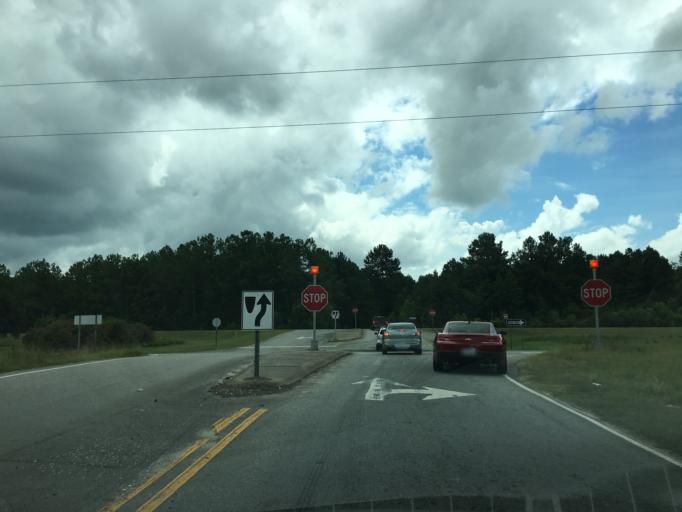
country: US
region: North Carolina
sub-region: Brunswick County
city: Carolina Shores
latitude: 33.9363
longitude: -78.5683
